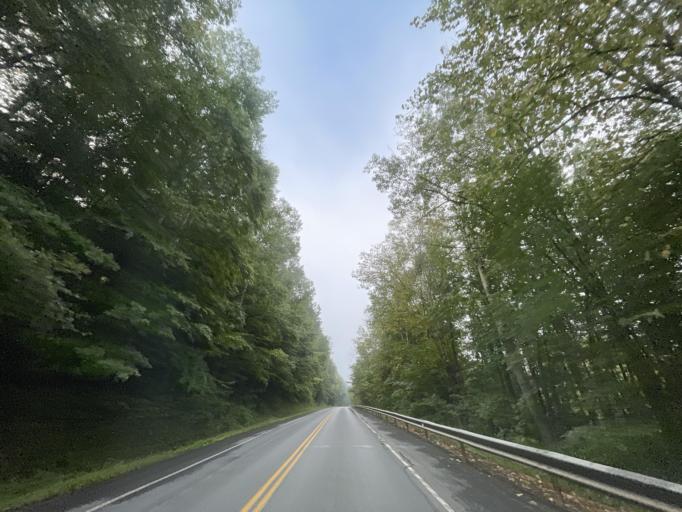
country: US
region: New York
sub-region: Chenango County
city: Oxford
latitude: 42.3811
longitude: -75.6283
